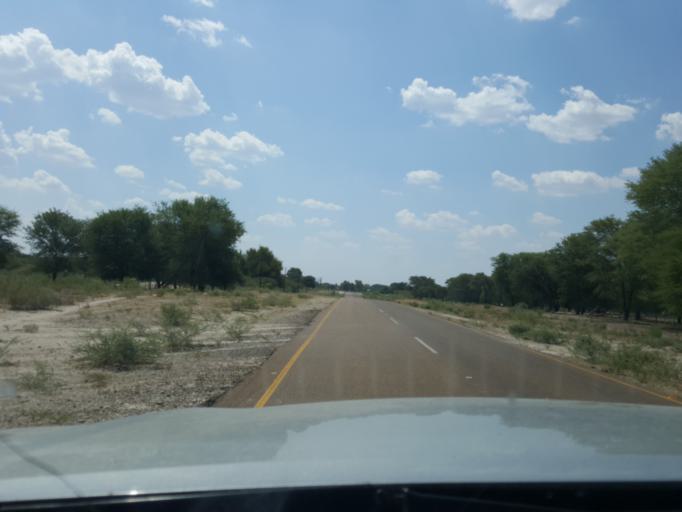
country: BW
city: Nokaneng
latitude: -19.6774
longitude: 22.1953
